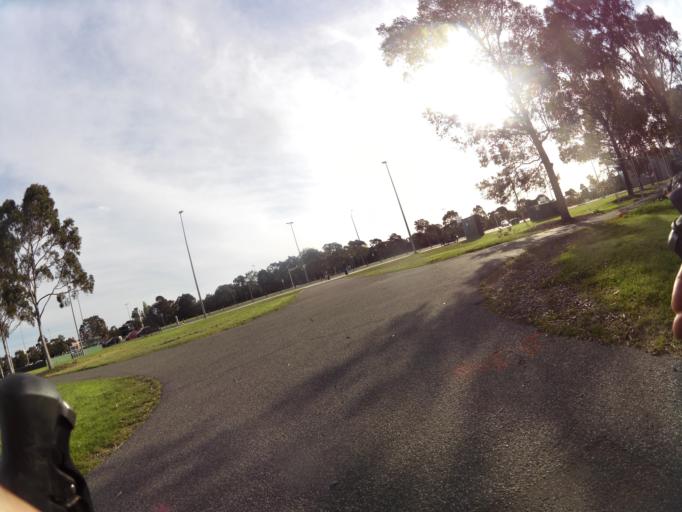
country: AU
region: Victoria
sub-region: Port Phillip
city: St Kilda West
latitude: -37.8515
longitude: 144.9721
